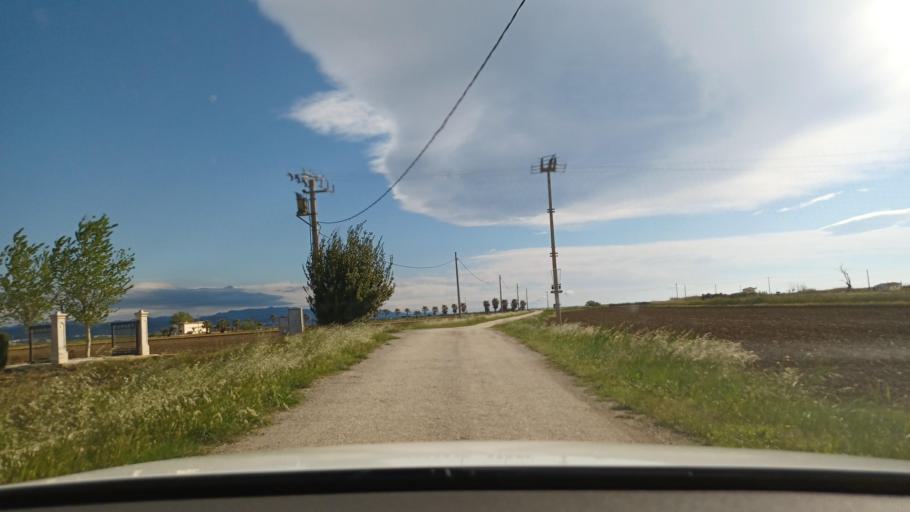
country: ES
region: Catalonia
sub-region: Provincia de Tarragona
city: L'Ampolla
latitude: 40.7758
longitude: 0.7121
